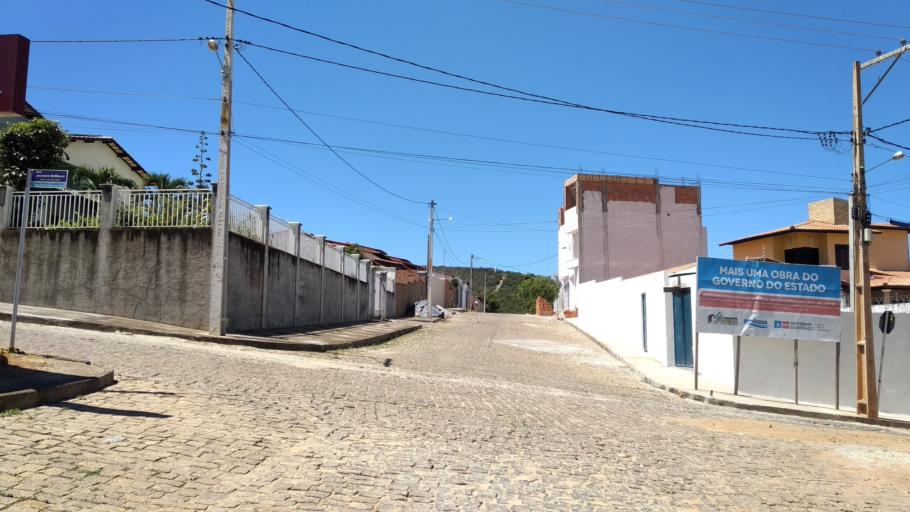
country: BR
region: Bahia
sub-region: Caetite
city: Caetite
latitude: -14.0736
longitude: -42.4805
